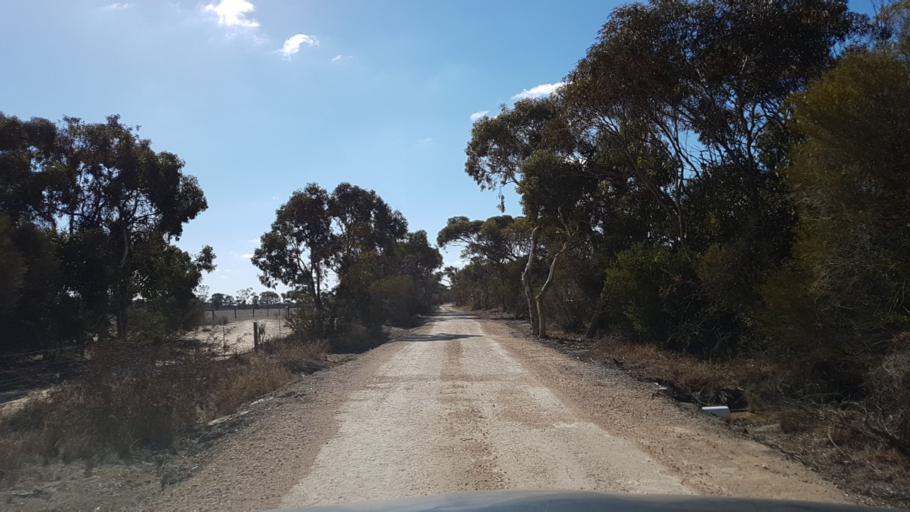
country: AU
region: South Australia
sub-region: Alexandrina
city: Goolwa
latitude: -35.3790
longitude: 138.8303
